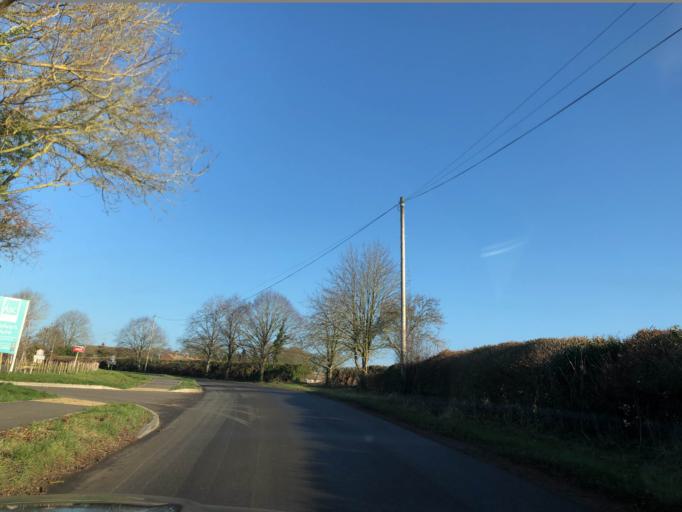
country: GB
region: England
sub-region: Warwickshire
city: Harbury
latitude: 52.1967
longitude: -1.5070
